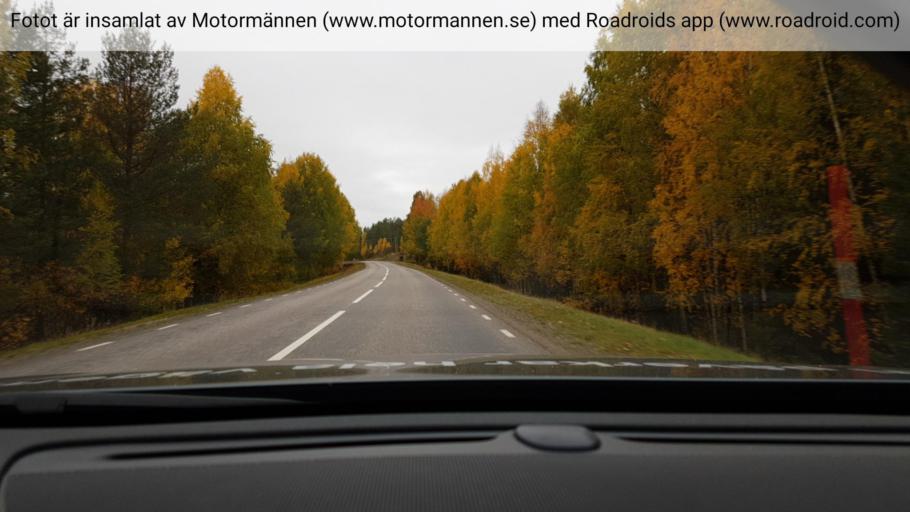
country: SE
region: Norrbotten
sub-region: Overkalix Kommun
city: OEverkalix
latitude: 66.5138
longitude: 22.7660
